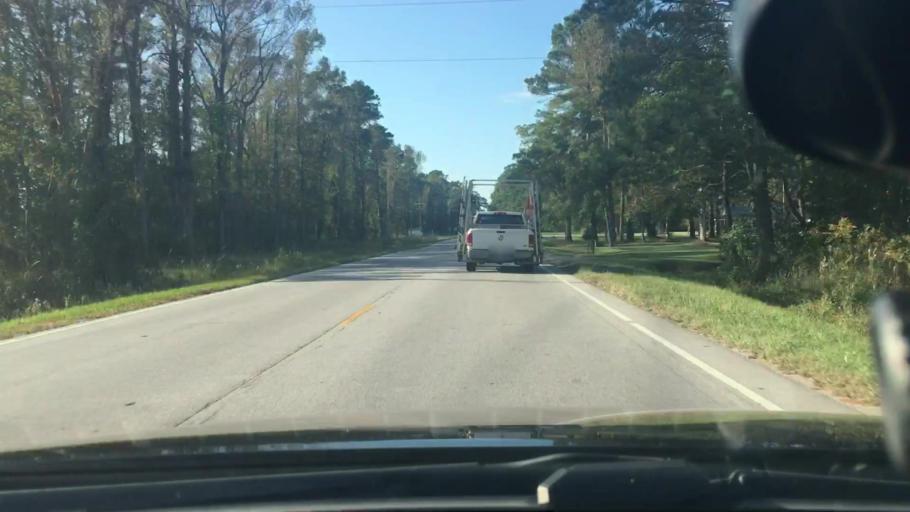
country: US
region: North Carolina
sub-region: Craven County
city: Vanceboro
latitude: 35.2603
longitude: -77.1004
